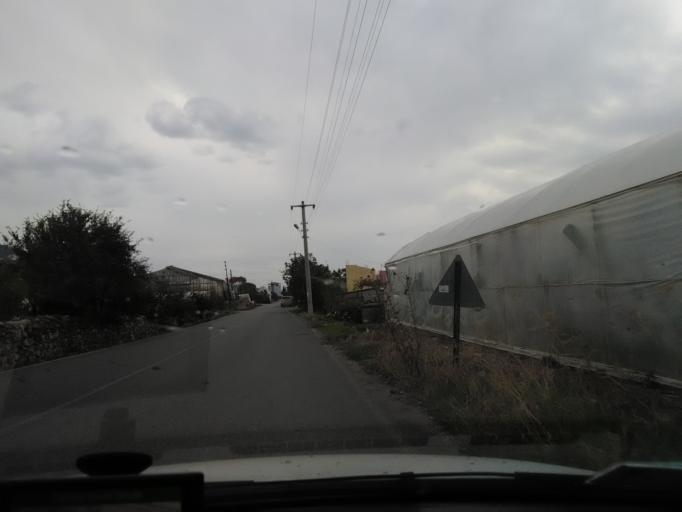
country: TR
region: Antalya
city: Gazipasa
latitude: 36.2566
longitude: 32.3054
